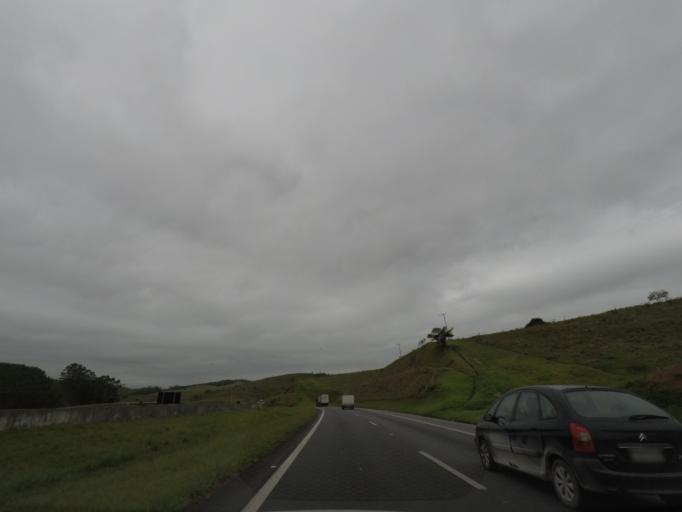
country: BR
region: Sao Paulo
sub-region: Santa Isabel
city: Santa Isabel
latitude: -23.2564
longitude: -46.1009
